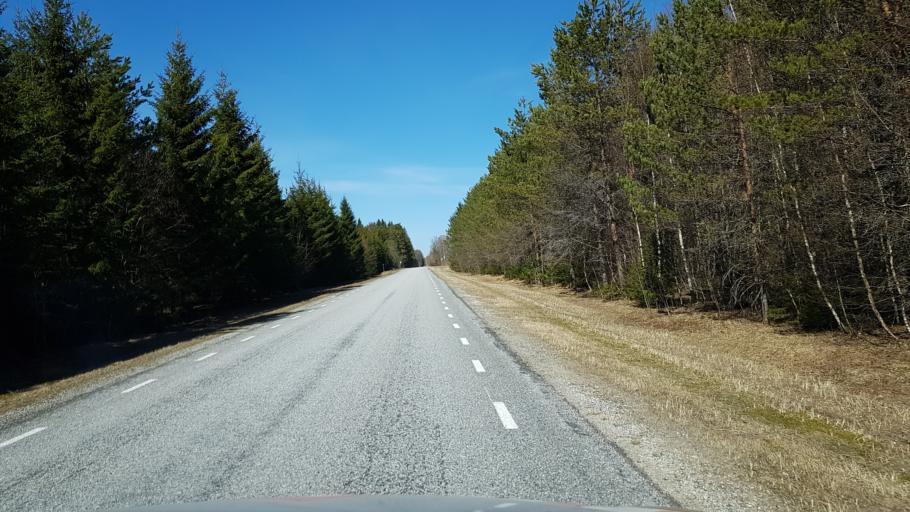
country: EE
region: Laeaene-Virumaa
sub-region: Vinni vald
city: Vinni
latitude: 59.1587
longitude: 26.5141
